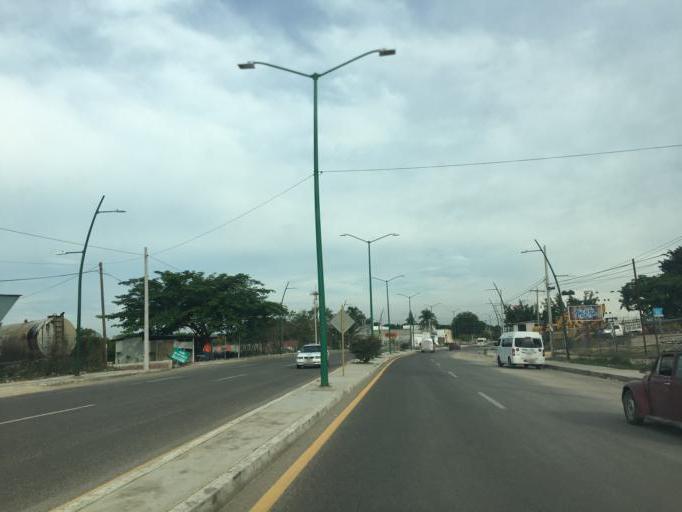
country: MX
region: Chiapas
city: Tuxtla Gutierrez
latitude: 16.7664
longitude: -93.1669
